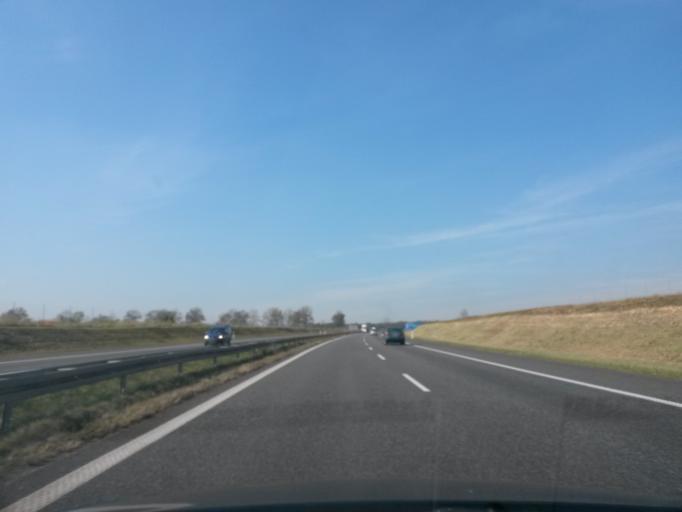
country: PL
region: Silesian Voivodeship
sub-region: Powiat gliwicki
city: Zernica
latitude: 50.2701
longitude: 18.5816
